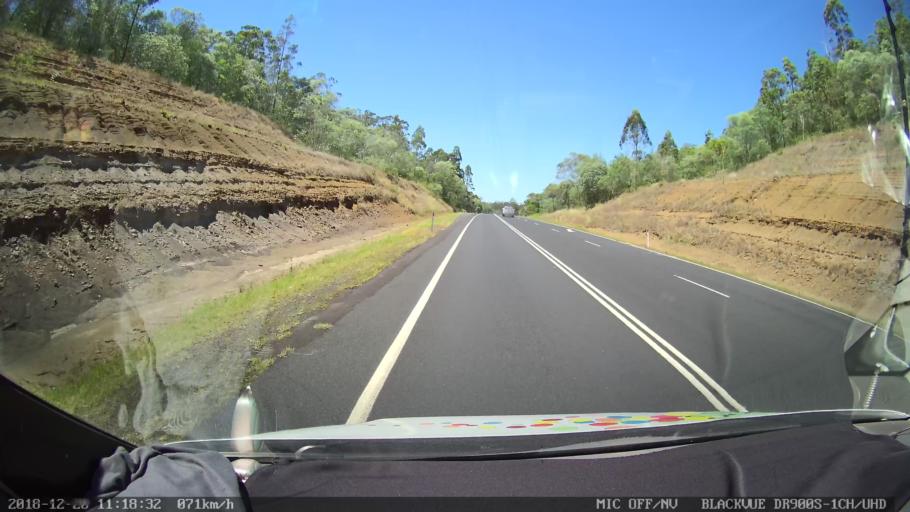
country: AU
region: New South Wales
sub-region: Richmond Valley
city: Casino
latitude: -29.0527
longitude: 153.0064
